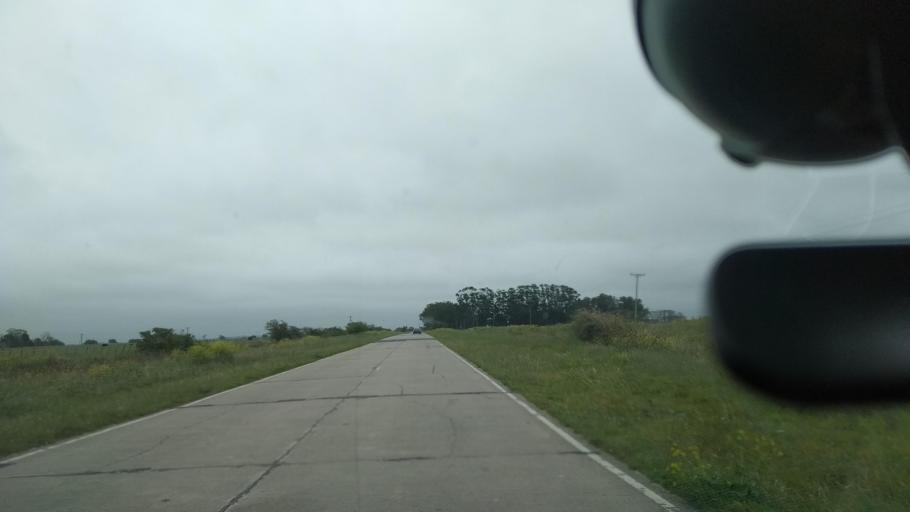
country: AR
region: Buenos Aires
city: Veronica
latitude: -35.5814
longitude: -57.2761
